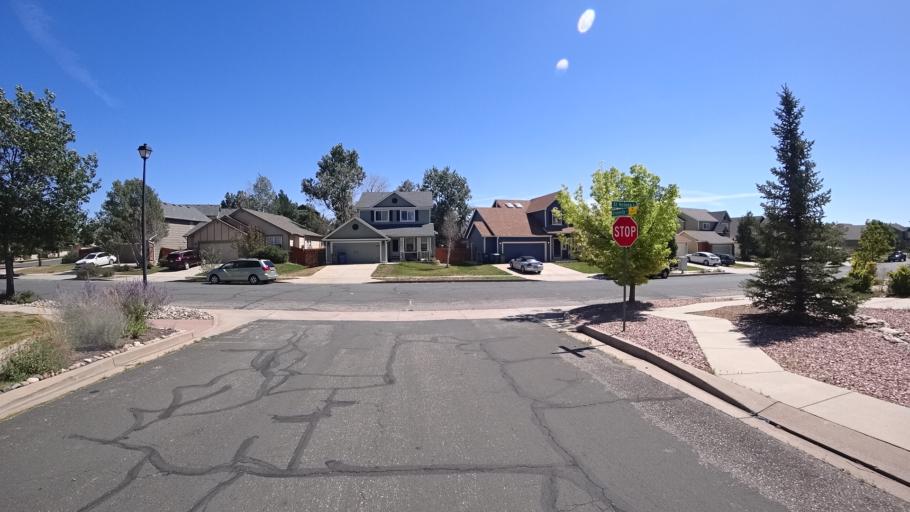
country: US
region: Colorado
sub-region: El Paso County
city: Black Forest
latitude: 38.9510
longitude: -104.7595
